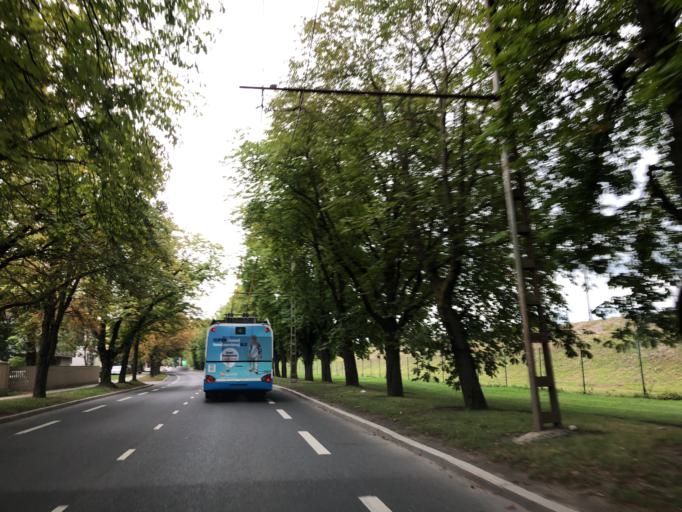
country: EE
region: Harju
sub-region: Tallinna linn
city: Tallinn
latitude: 59.4315
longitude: 24.7238
